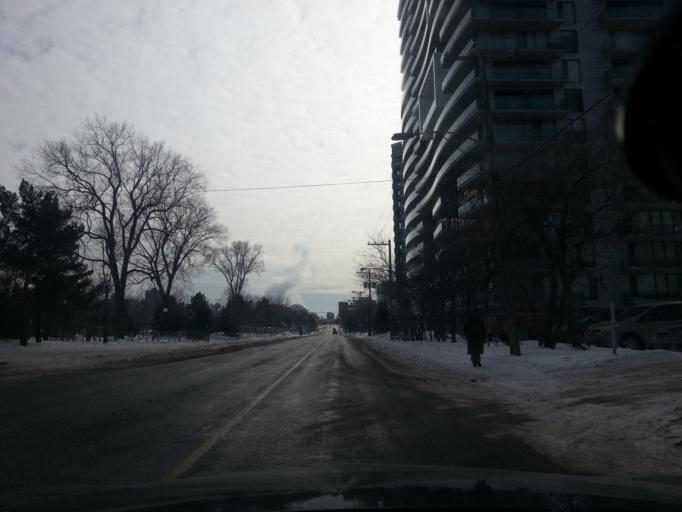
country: CA
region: Ontario
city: Ottawa
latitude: 45.4362
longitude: -75.7089
